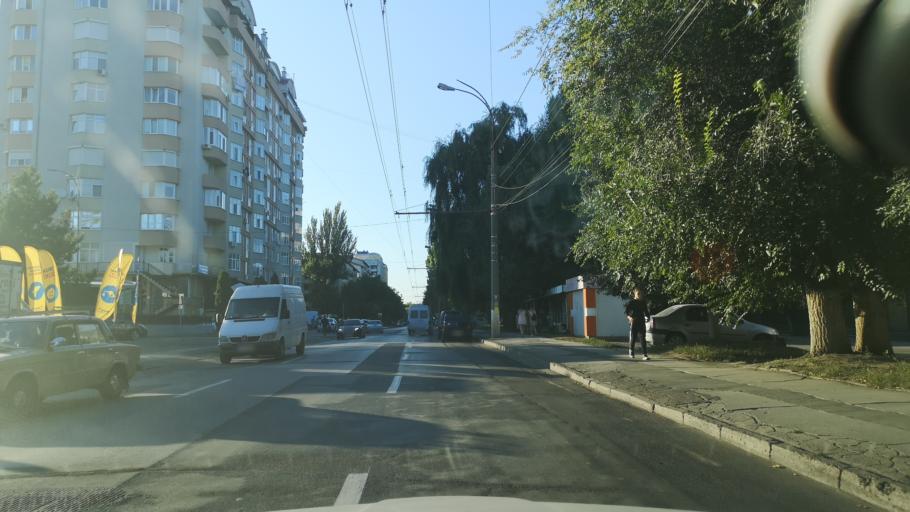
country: MD
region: Chisinau
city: Chisinau
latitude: 46.9854
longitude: 28.8752
